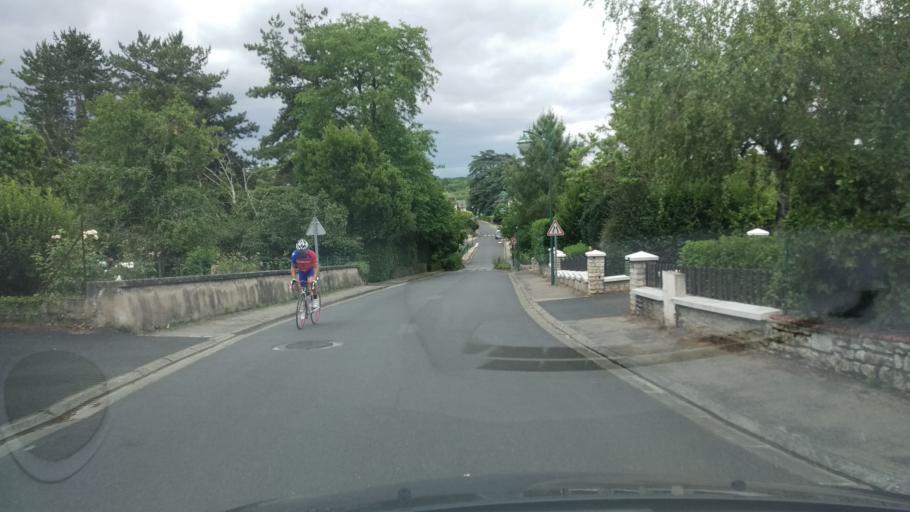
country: FR
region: Poitou-Charentes
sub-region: Departement de la Vienne
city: Vouneuil-sous-Biard
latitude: 46.5744
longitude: 0.2730
